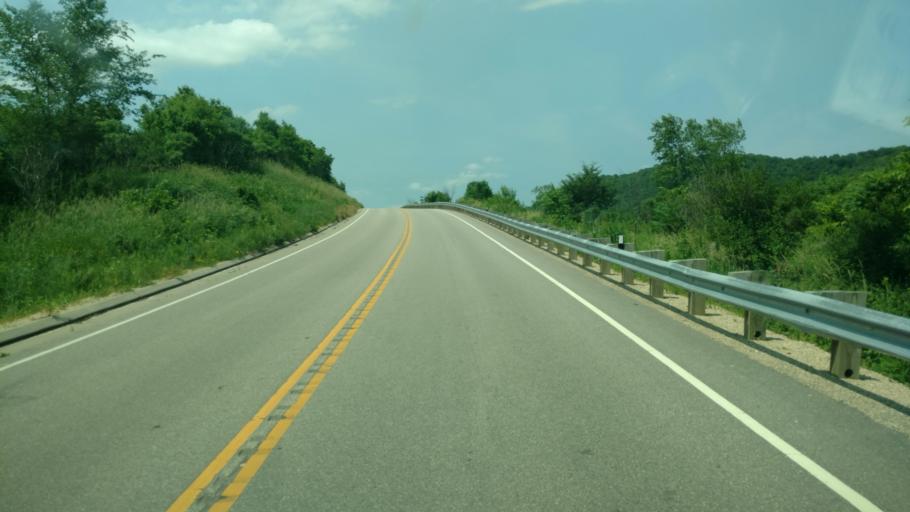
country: US
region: Wisconsin
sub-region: Vernon County
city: Viroqua
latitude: 43.5345
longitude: -90.6633
